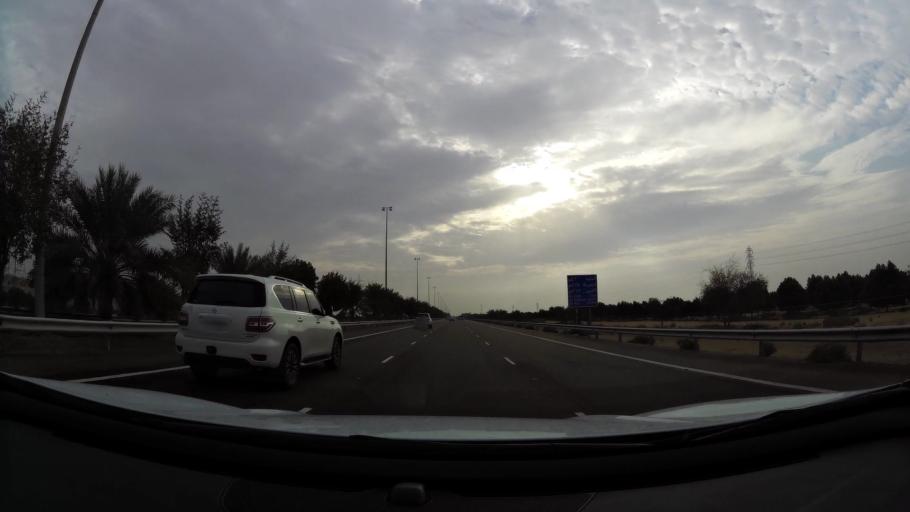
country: AE
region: Abu Dhabi
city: Abu Dhabi
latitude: 24.2265
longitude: 54.7953
